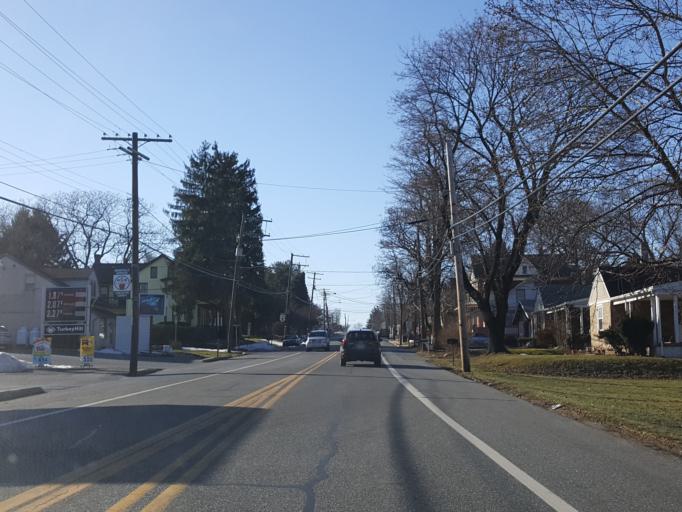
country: US
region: Pennsylvania
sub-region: Lancaster County
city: Mountville
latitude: 40.0376
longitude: -76.4211
